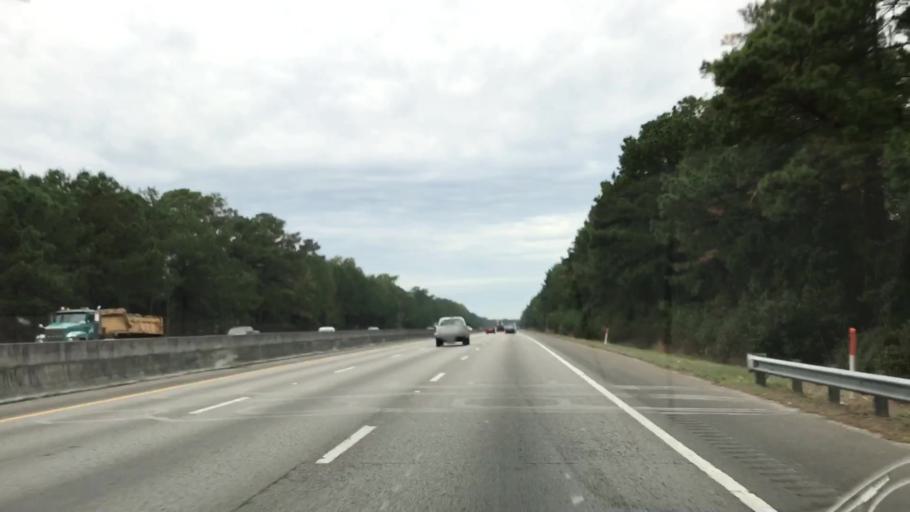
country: US
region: South Carolina
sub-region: Berkeley County
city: Goose Creek
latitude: 32.9500
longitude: -80.0597
